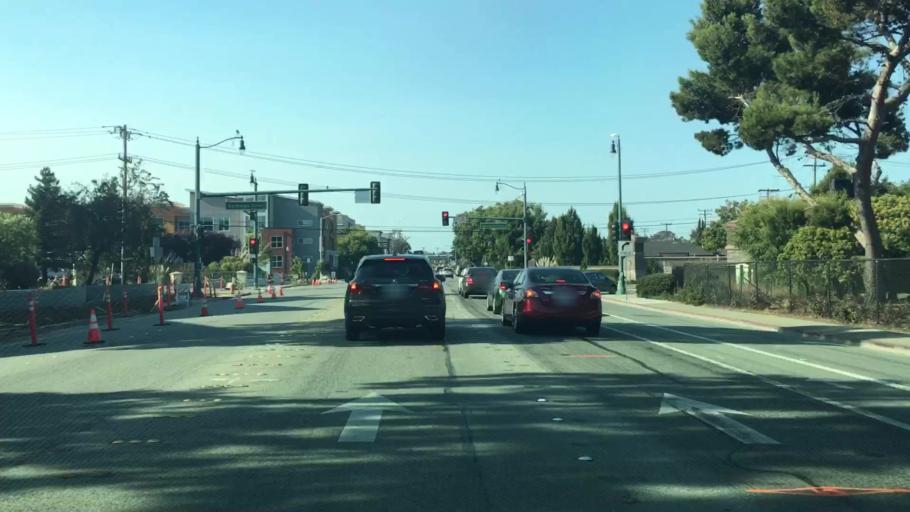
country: US
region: California
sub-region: San Mateo County
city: San Mateo
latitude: 37.5480
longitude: -122.3047
